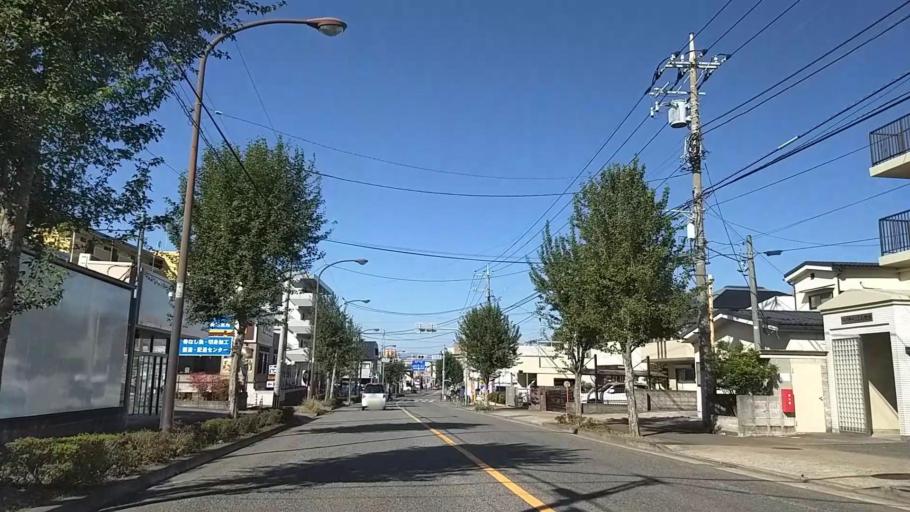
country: JP
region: Tokyo
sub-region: Machida-shi
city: Machida
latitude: 35.5757
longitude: 139.4163
